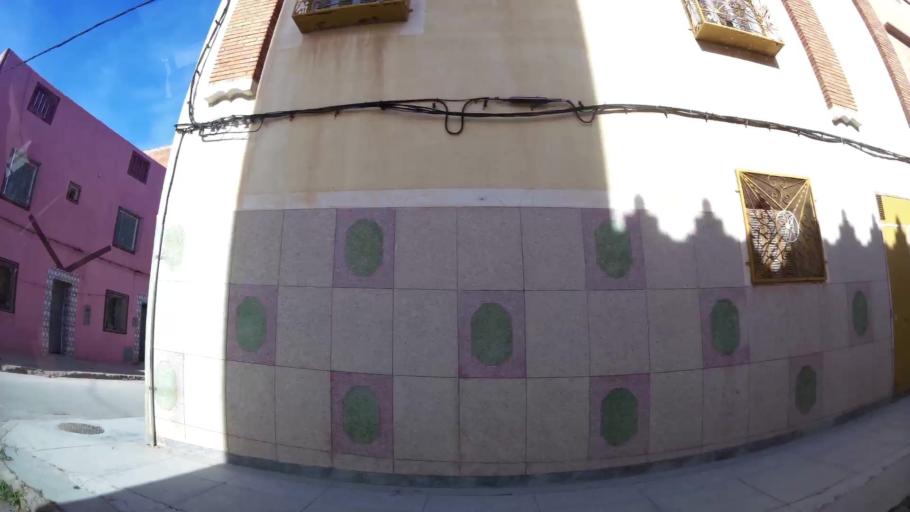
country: MA
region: Oriental
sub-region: Oujda-Angad
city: Oujda
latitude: 34.6728
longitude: -1.8956
